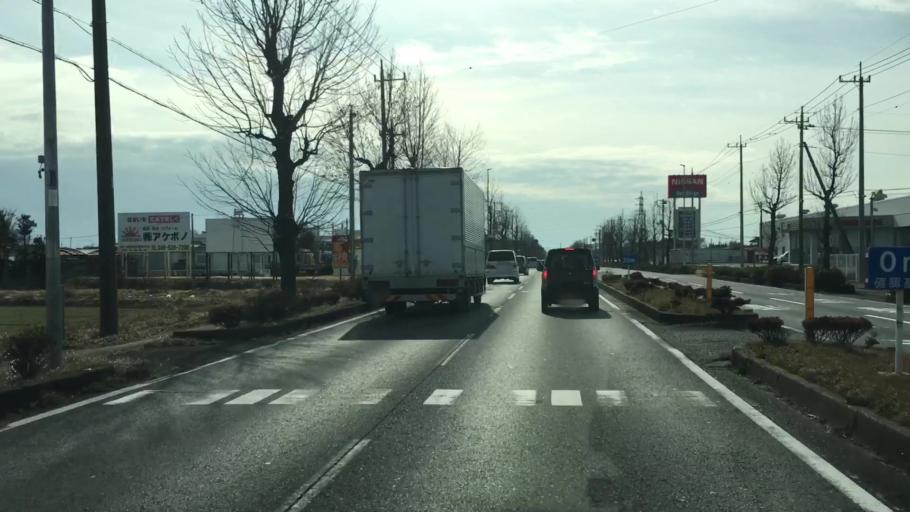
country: JP
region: Saitama
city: Menuma
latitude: 36.1943
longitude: 139.3704
